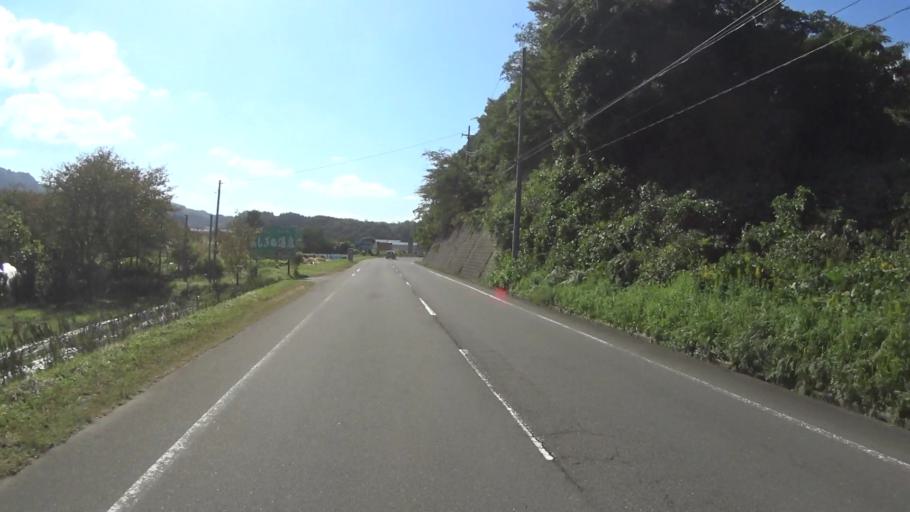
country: JP
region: Kyoto
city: Miyazu
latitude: 35.6456
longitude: 135.0844
